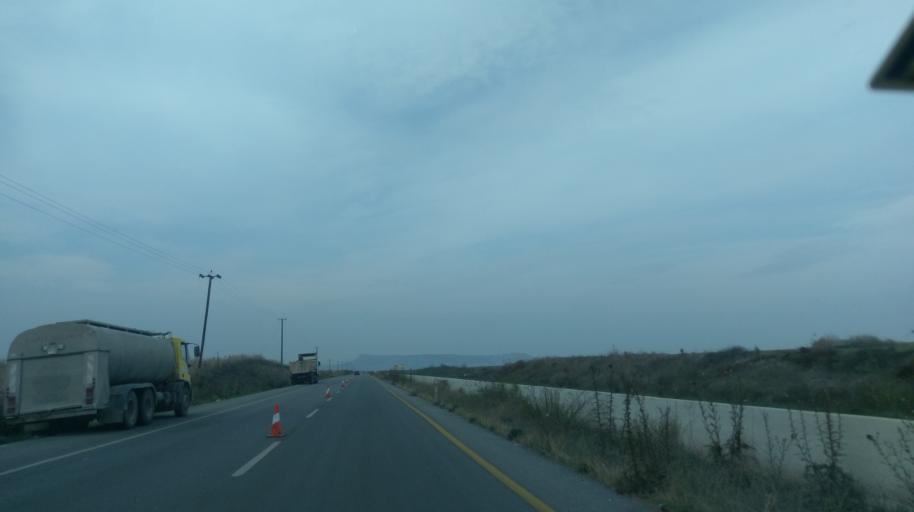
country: CY
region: Lefkosia
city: Mammari
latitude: 35.2111
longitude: 33.2140
